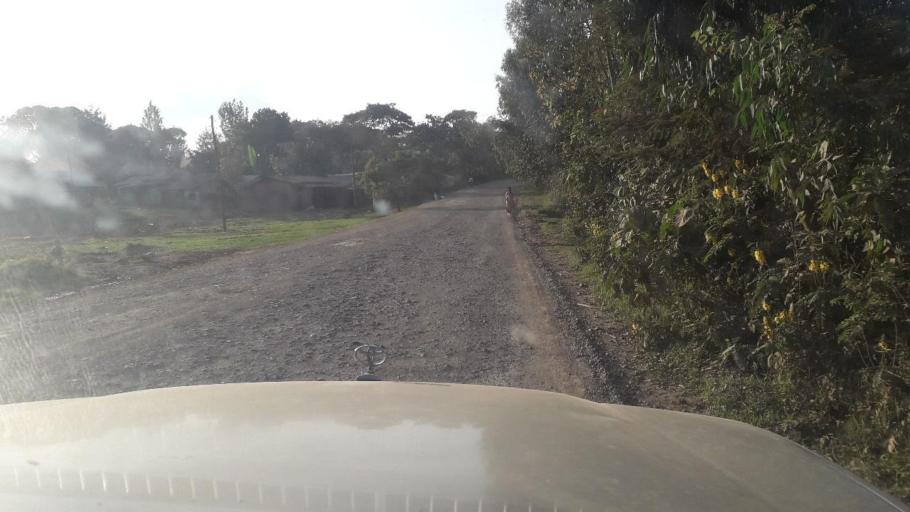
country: ET
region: Oromiya
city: Jima
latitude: 7.5964
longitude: 36.8478
